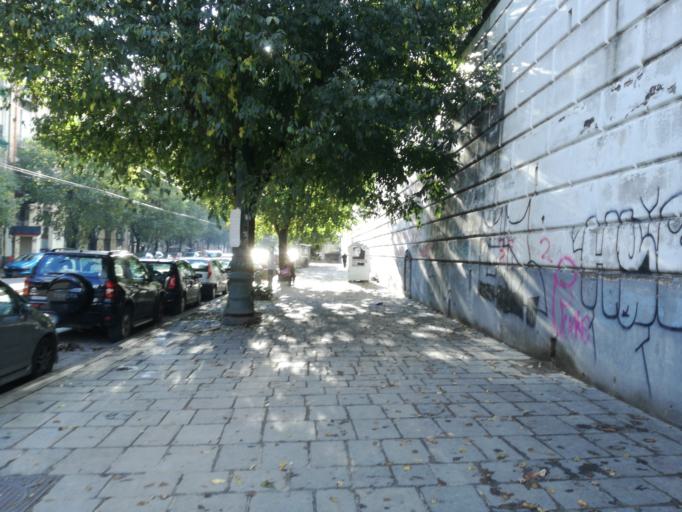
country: IT
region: Campania
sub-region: Provincia di Napoli
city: Napoli
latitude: 40.8613
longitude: 14.2644
